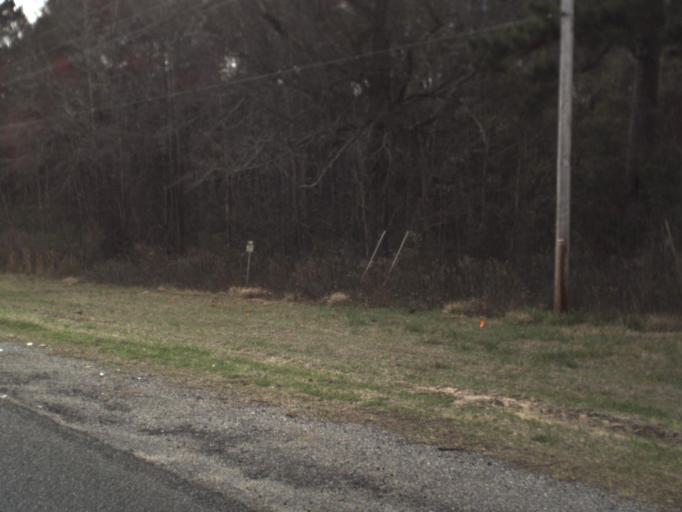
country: US
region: Florida
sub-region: Jackson County
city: Marianna
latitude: 30.7607
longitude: -85.3784
